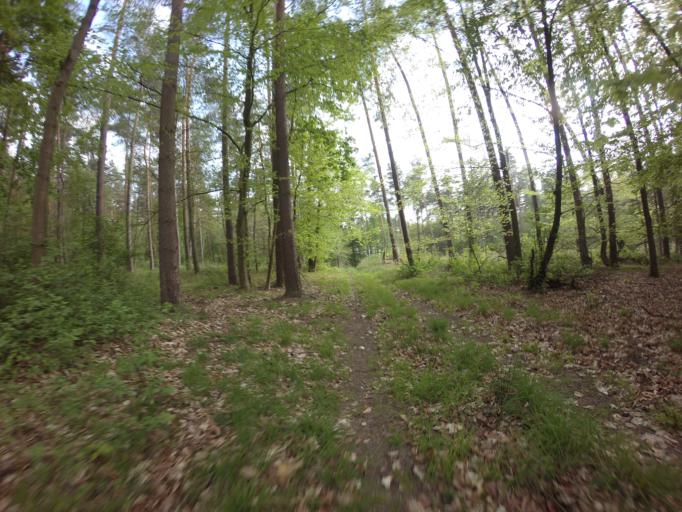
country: PL
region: West Pomeranian Voivodeship
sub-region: Powiat choszczenski
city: Choszczno
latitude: 53.1536
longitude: 15.3286
